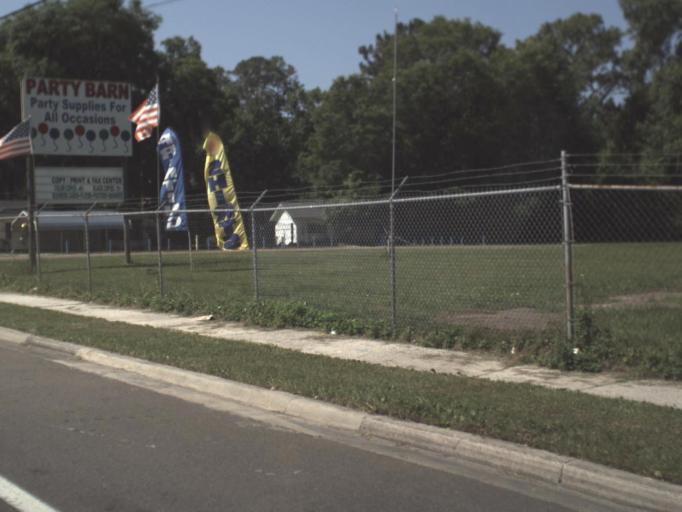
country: US
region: Florida
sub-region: Duval County
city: Jacksonville
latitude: 30.4347
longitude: -81.6959
